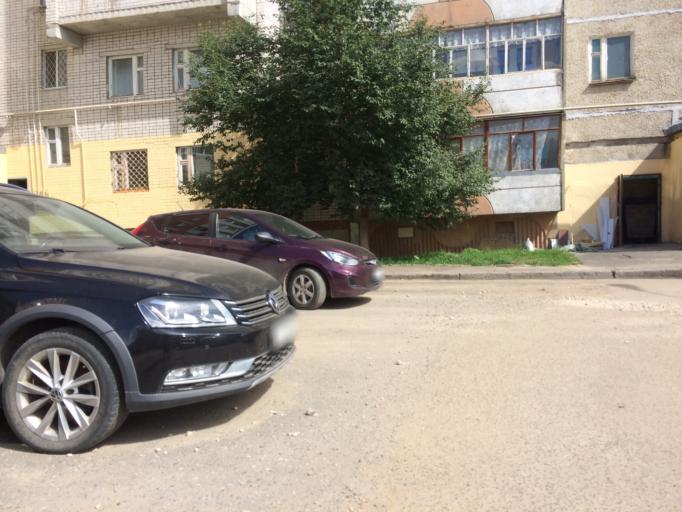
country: RU
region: Mariy-El
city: Yoshkar-Ola
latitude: 56.6362
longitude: 47.9313
